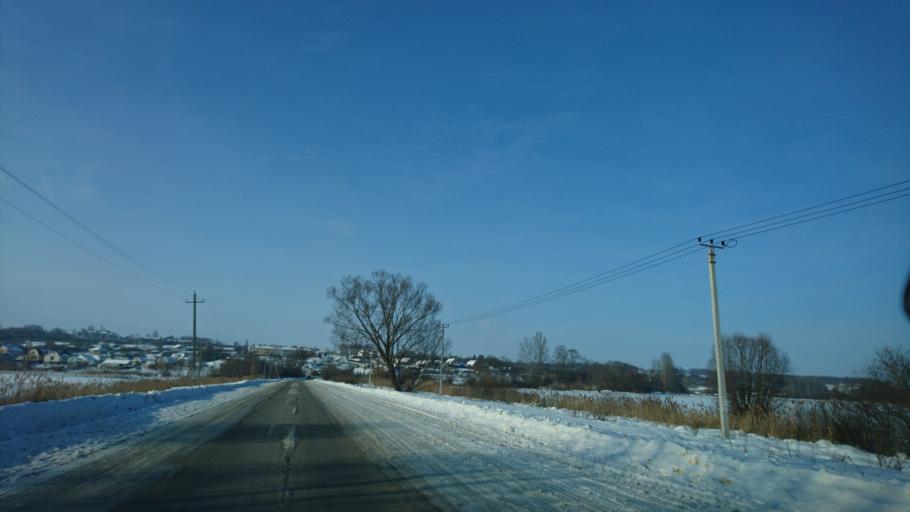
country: RU
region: Belgorod
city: Severnyy
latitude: 50.7273
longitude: 36.6084
